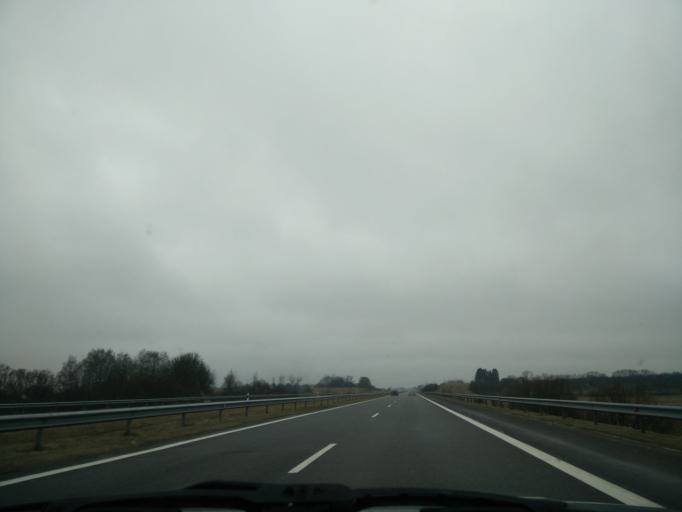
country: LT
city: Skaudvile
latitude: 55.4458
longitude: 22.7210
